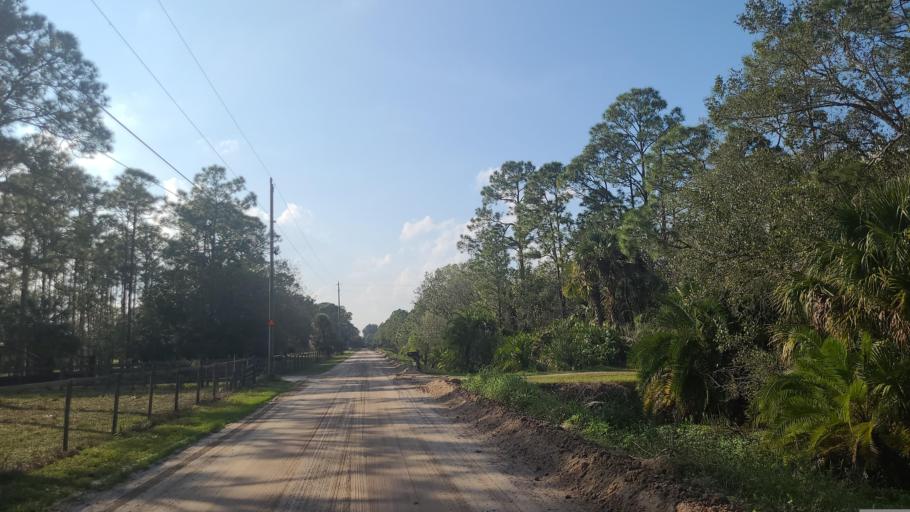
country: US
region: Florida
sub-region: Indian River County
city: Fellsmere
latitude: 27.7538
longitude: -80.6067
